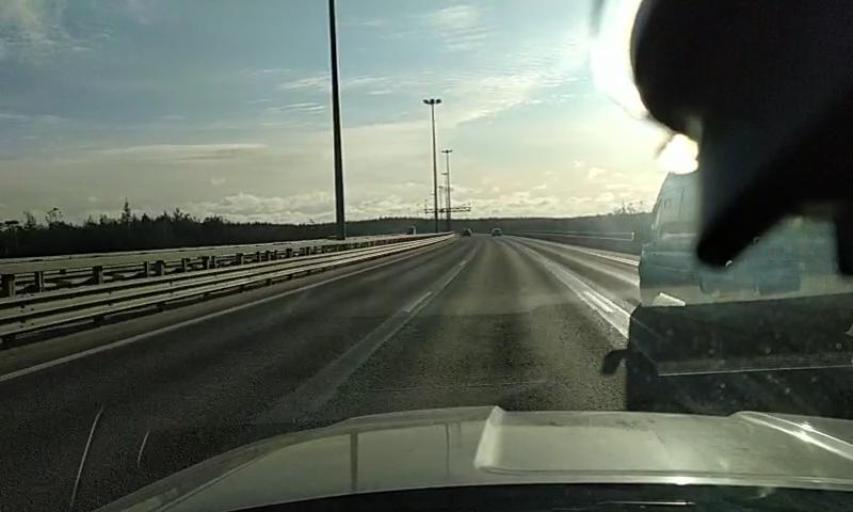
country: RU
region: St.-Petersburg
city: Pesochnyy
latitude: 60.0876
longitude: 30.1013
